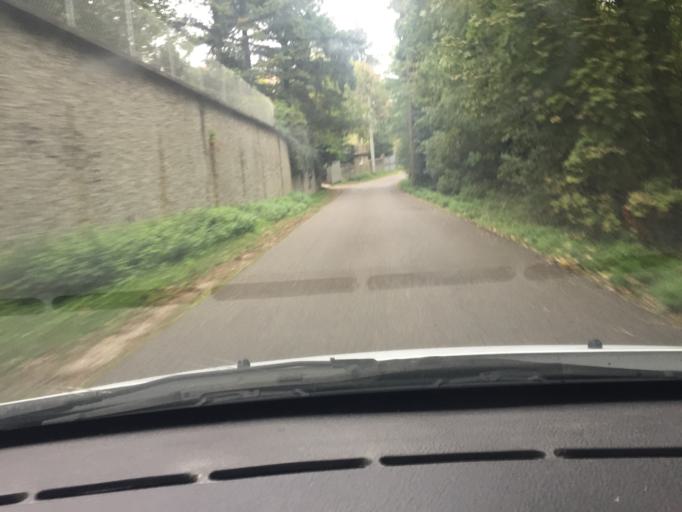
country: FR
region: Rhone-Alpes
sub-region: Departement du Rhone
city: Sathonay-Camp
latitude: 45.8087
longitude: 4.8806
